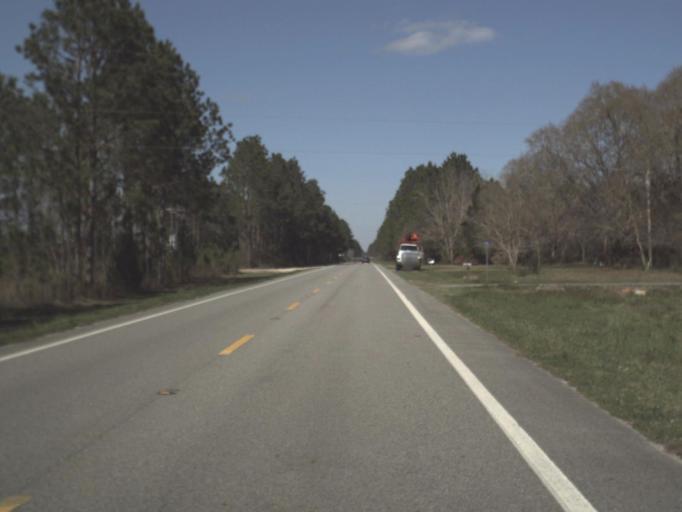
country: US
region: Florida
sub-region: Gulf County
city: Port Saint Joe
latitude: 29.9376
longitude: -85.1892
